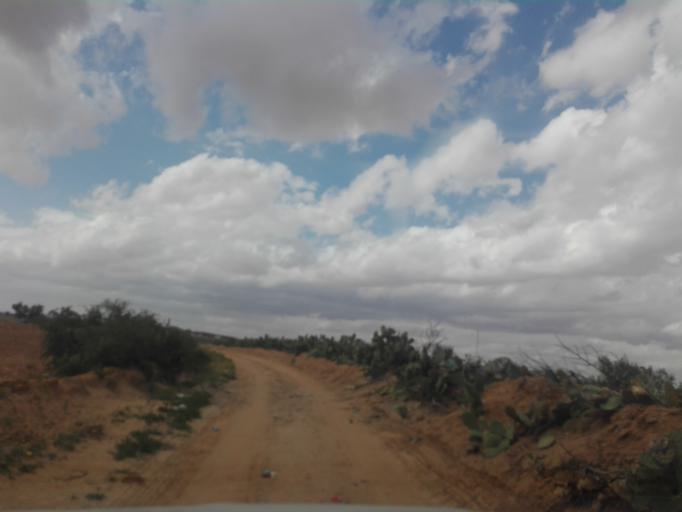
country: TN
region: Safaqis
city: Sfax
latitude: 34.6963
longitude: 10.4452
